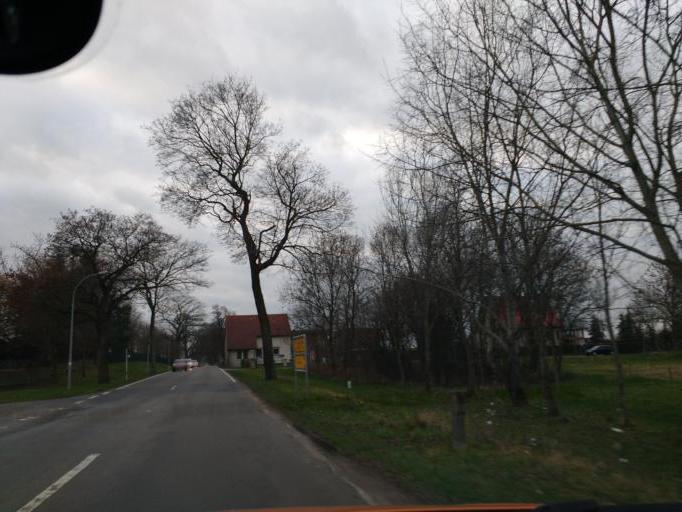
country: DE
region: Brandenburg
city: Wriezen
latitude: 52.6858
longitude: 14.0968
